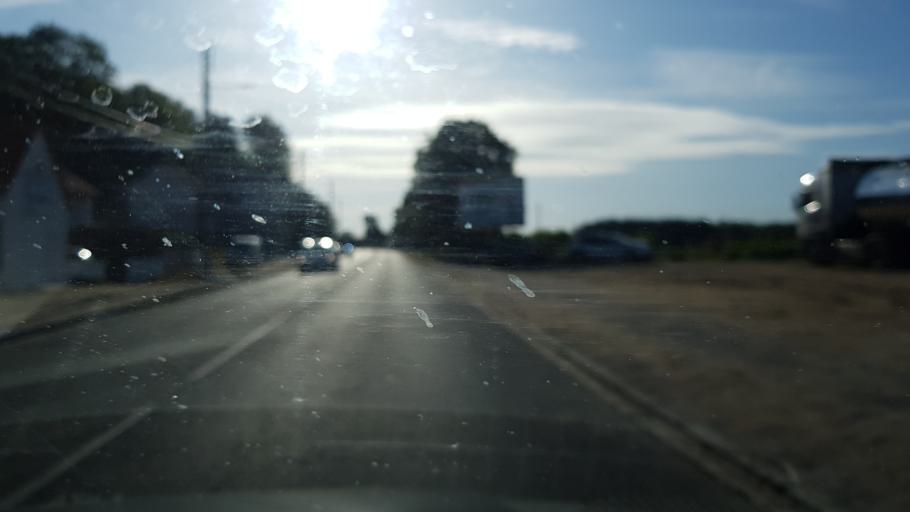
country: FR
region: Centre
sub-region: Departement du Loiret
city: Gien
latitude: 47.6785
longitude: 2.6470
